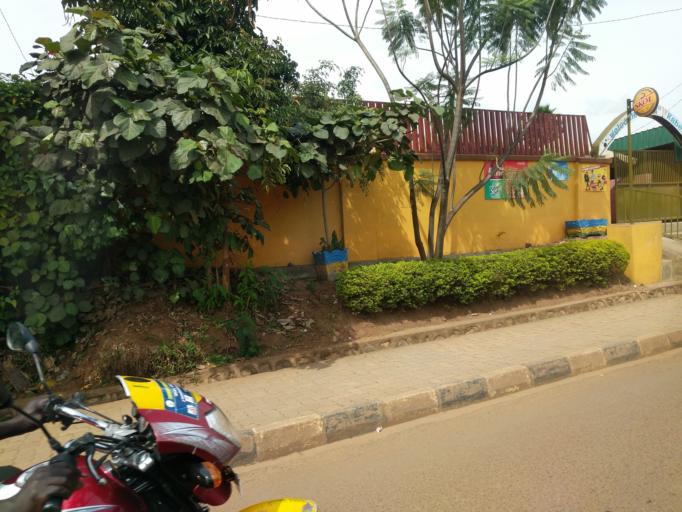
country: RW
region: Kigali
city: Kigali
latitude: -1.9709
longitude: 30.1236
